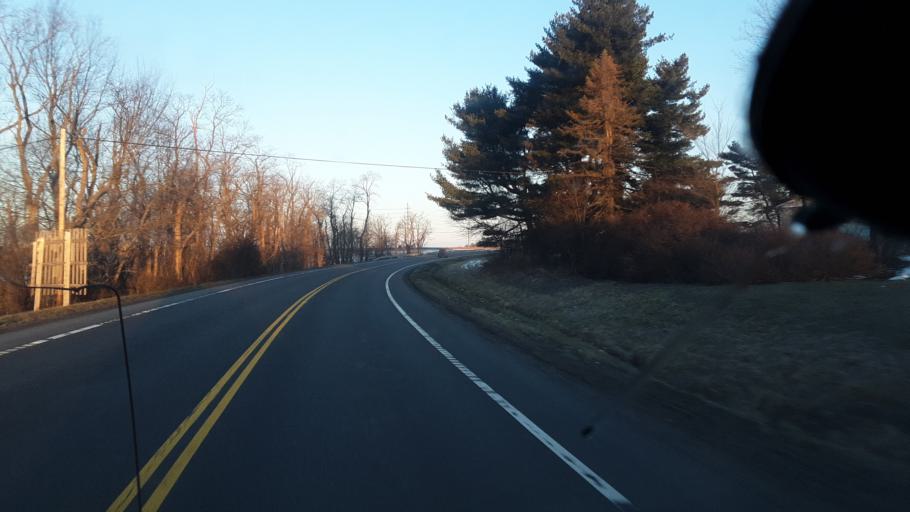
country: US
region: Ohio
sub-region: Perry County
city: Somerset
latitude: 39.8141
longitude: -82.3155
